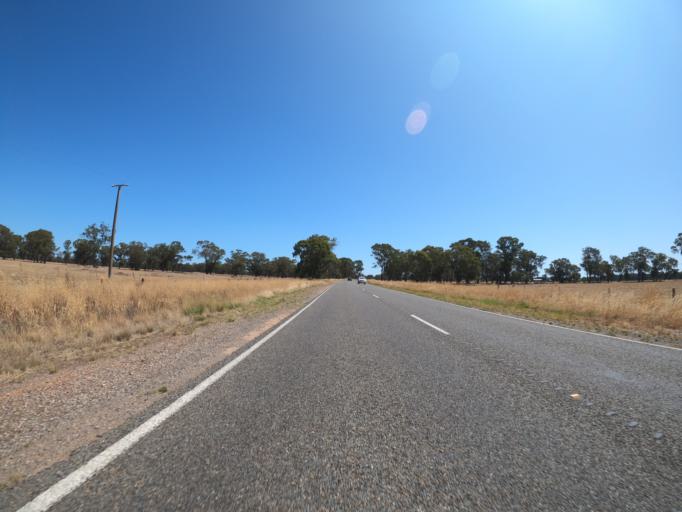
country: AU
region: New South Wales
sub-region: Corowa Shire
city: Corowa
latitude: -36.0825
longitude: 146.3357
